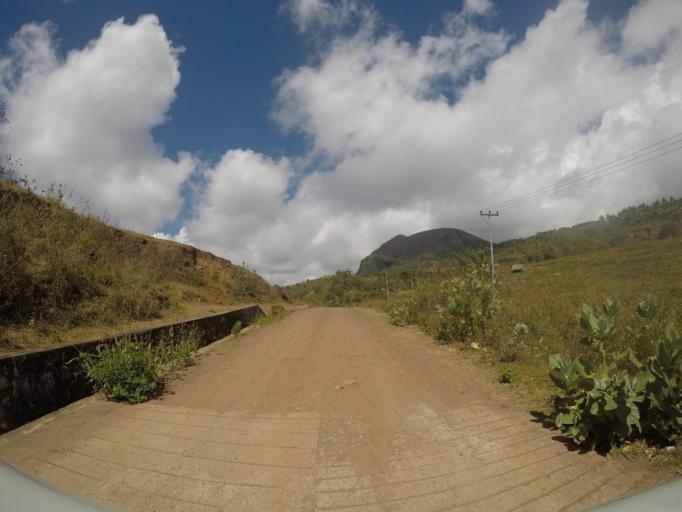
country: TL
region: Lautem
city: Lospalos
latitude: -8.5382
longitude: 126.8055
